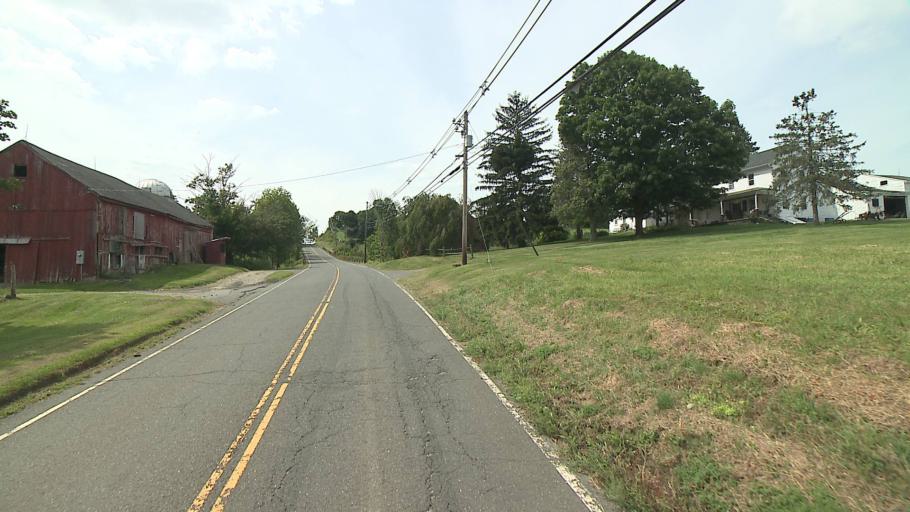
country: US
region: Connecticut
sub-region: Litchfield County
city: Bethlehem Village
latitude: 41.6203
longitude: -73.2403
